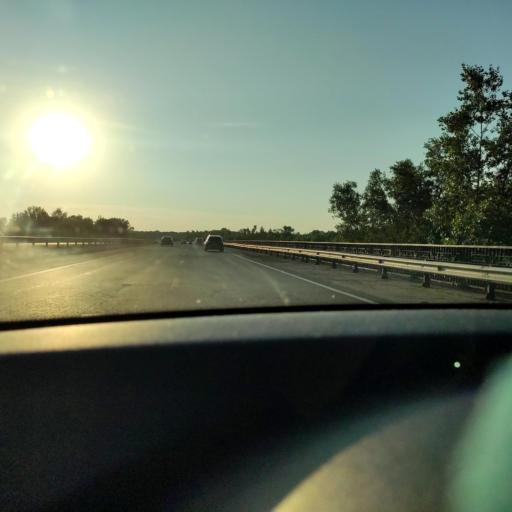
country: RU
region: Samara
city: Kinel'
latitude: 53.2570
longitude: 50.5791
